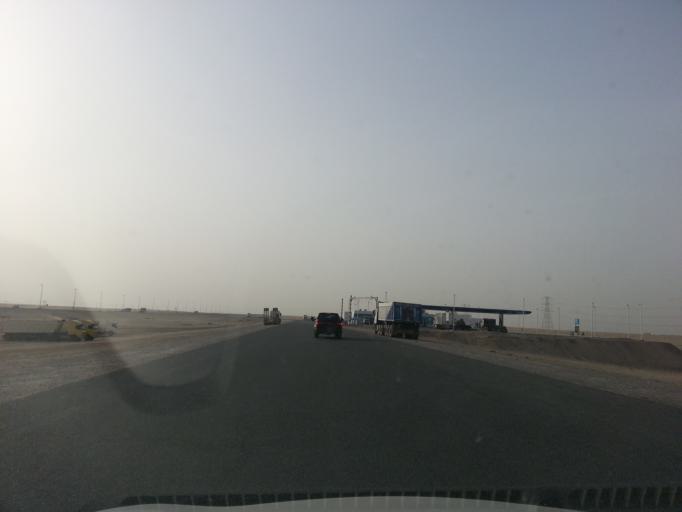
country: AE
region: Dubai
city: Dubai
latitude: 24.8044
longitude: 55.0707
